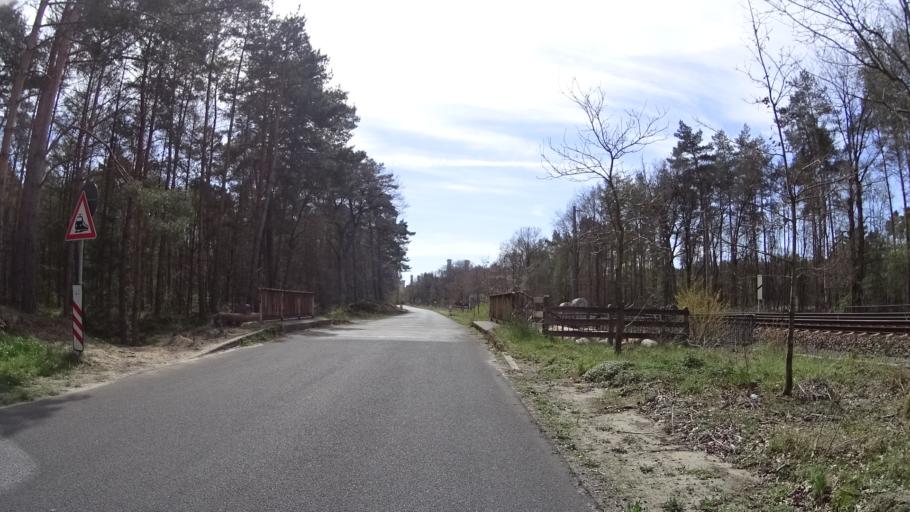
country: DE
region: Lower Saxony
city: Lingen
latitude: 52.4911
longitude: 7.3033
